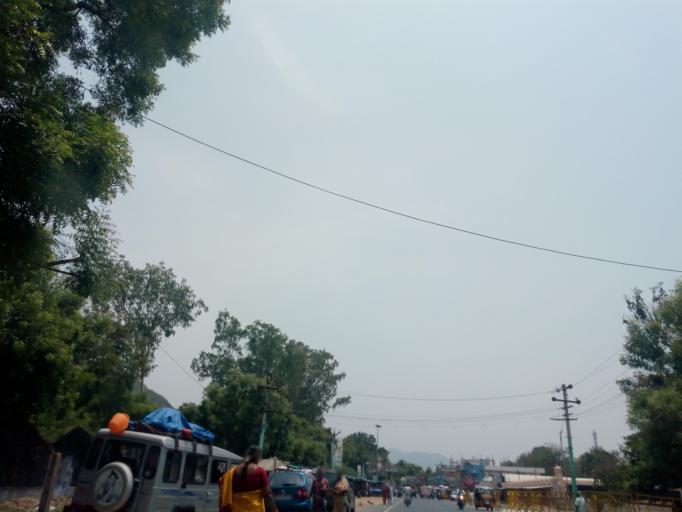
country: IN
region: Tamil Nadu
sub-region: Vellore
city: Vellore
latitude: 12.8700
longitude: 79.0892
